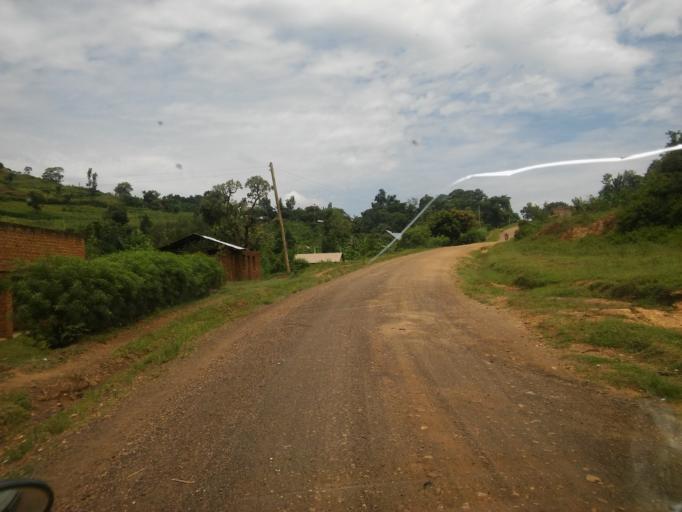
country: UG
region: Eastern Region
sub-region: Bududa District
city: Bududa
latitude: 0.9217
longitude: 34.2817
